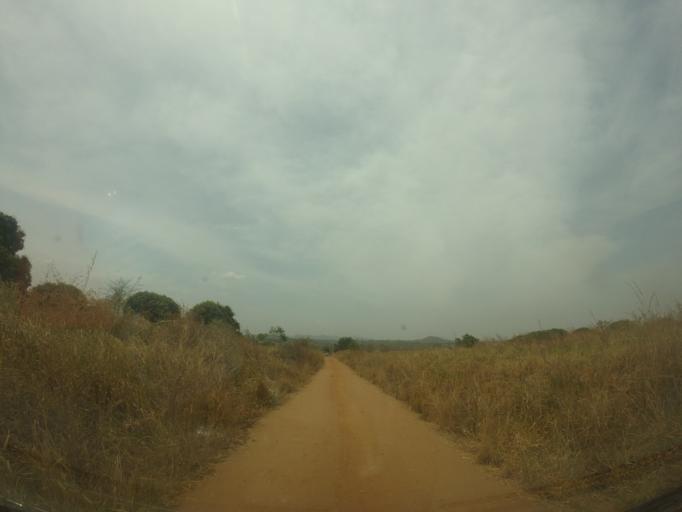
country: UG
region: Northern Region
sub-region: Nebbi District
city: Nebbi
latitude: 2.6211
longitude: 31.0415
